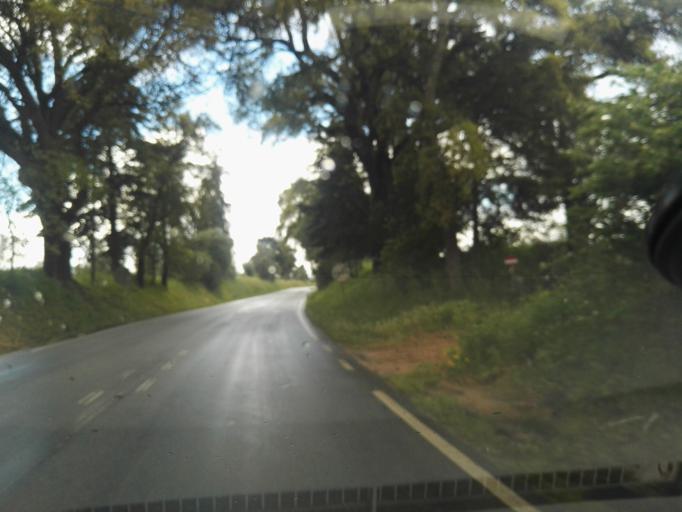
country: PT
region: Santarem
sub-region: Golega
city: Golega
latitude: 39.4165
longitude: -8.4952
